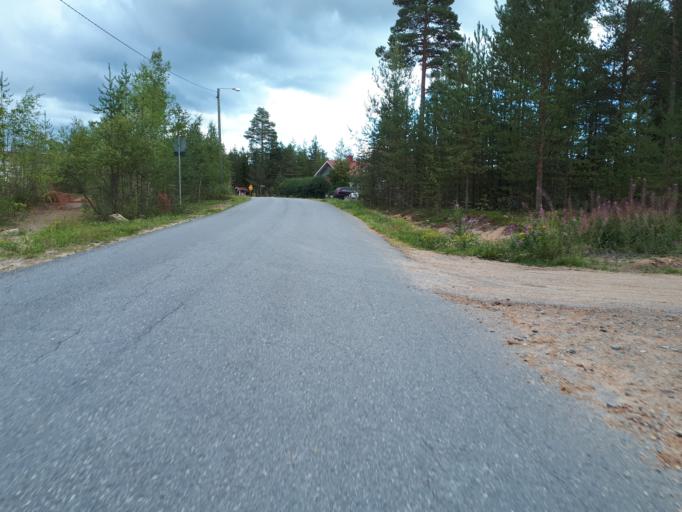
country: FI
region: Northern Ostrobothnia
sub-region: Oulunkaari
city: Ii
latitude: 65.3246
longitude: 25.3972
